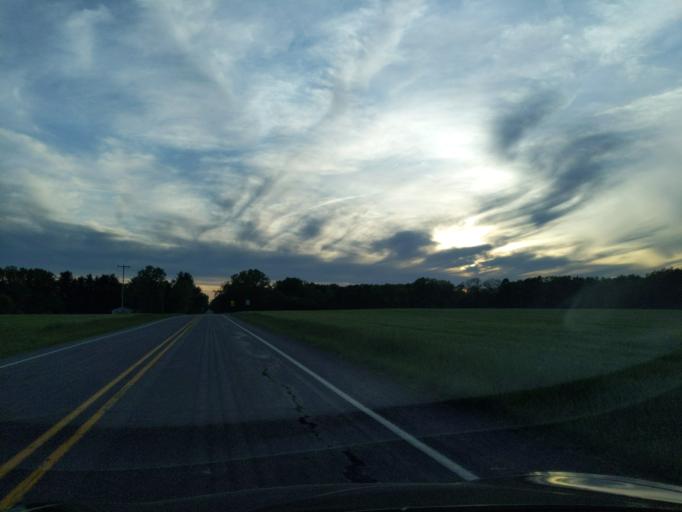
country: US
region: Michigan
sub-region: Ingham County
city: Williamston
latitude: 42.6009
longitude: -84.3246
